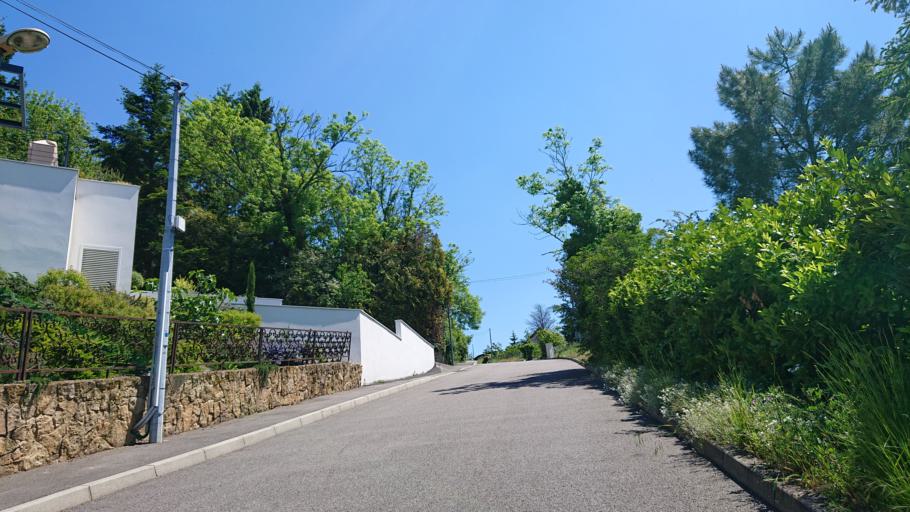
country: FR
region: Rhone-Alpes
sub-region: Departement de la Loire
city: Villars
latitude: 45.4612
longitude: 4.3468
